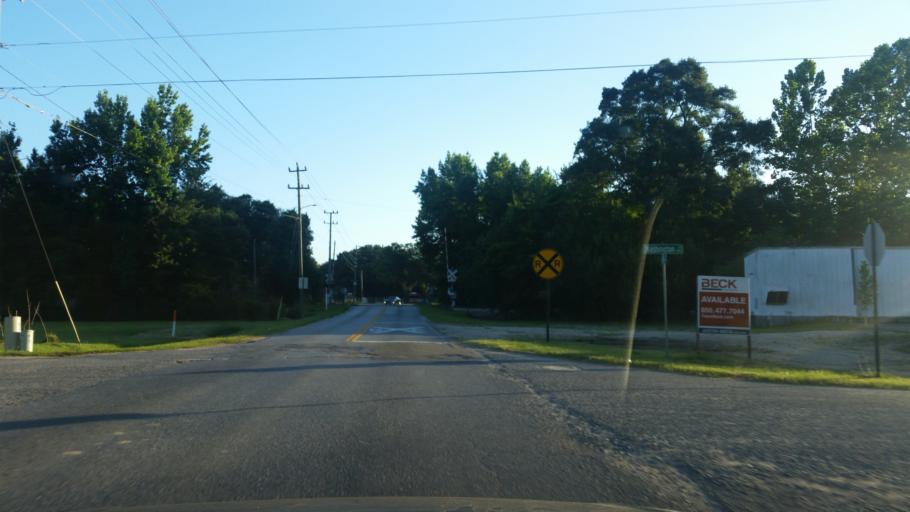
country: US
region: Florida
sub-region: Escambia County
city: Cantonment
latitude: 30.6063
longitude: -87.3318
